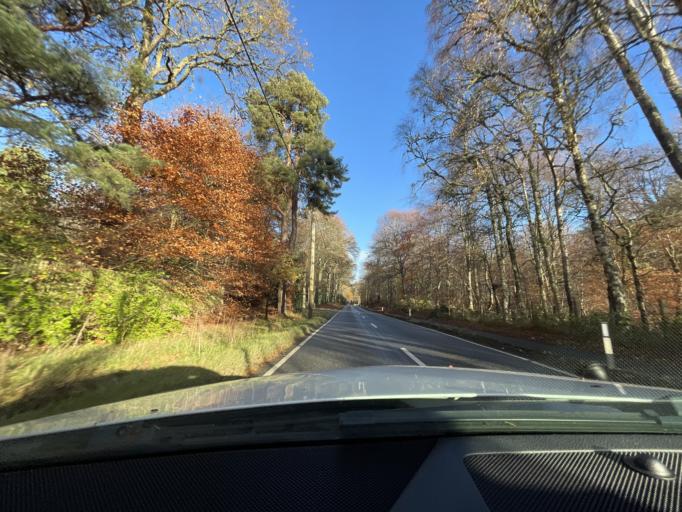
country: GB
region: Scotland
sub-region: Highland
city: Inverness
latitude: 57.4295
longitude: -4.2816
